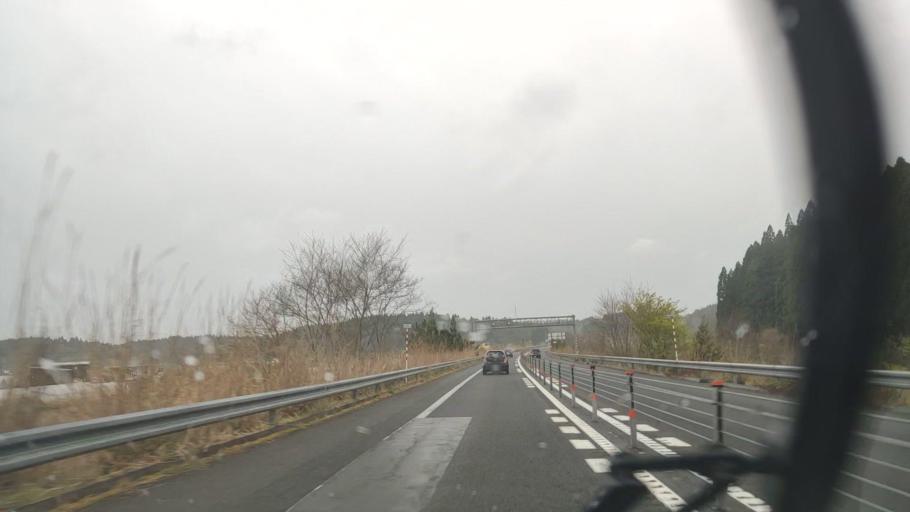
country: JP
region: Akita
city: Noshiromachi
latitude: 40.1882
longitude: 140.1011
